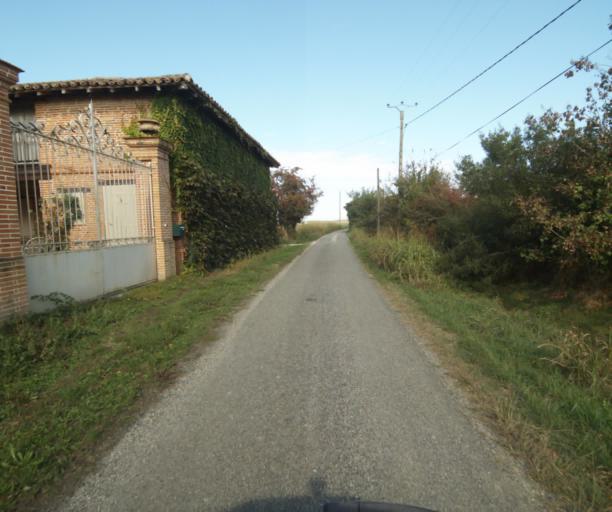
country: FR
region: Midi-Pyrenees
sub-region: Departement du Tarn-et-Garonne
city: Finhan
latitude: 43.8831
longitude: 1.2221
